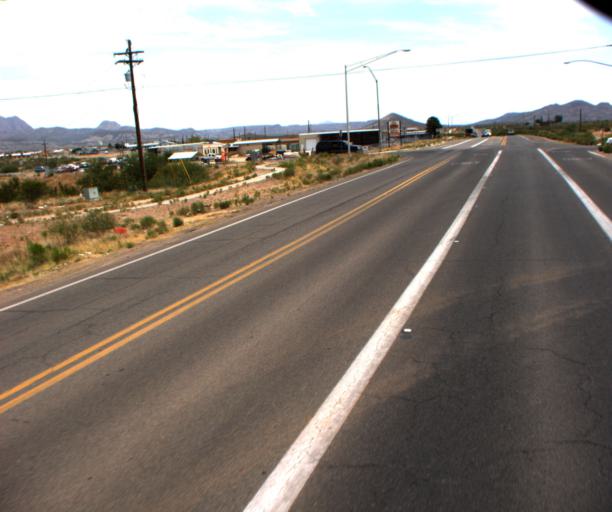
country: US
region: Arizona
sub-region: Gila County
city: Peridot
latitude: 33.2932
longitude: -110.4385
